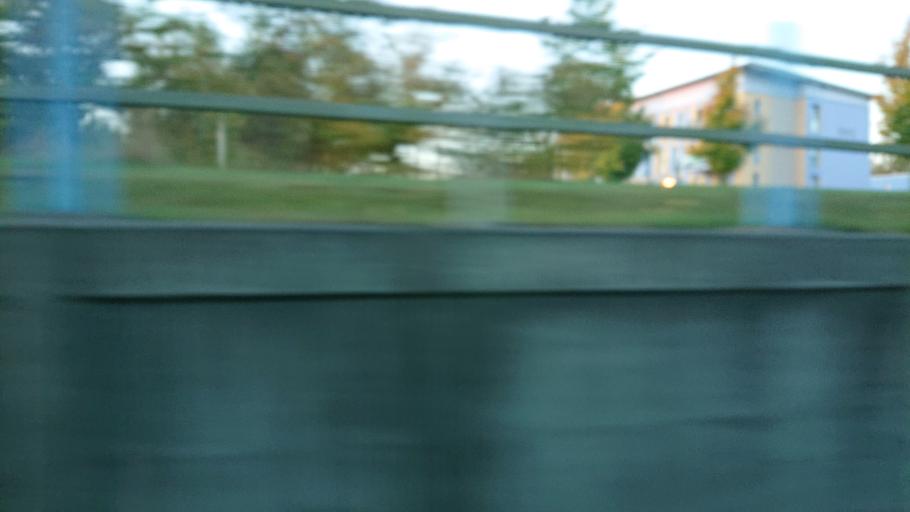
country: DE
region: Mecklenburg-Vorpommern
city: Greifswald
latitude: 54.0917
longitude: 13.3702
